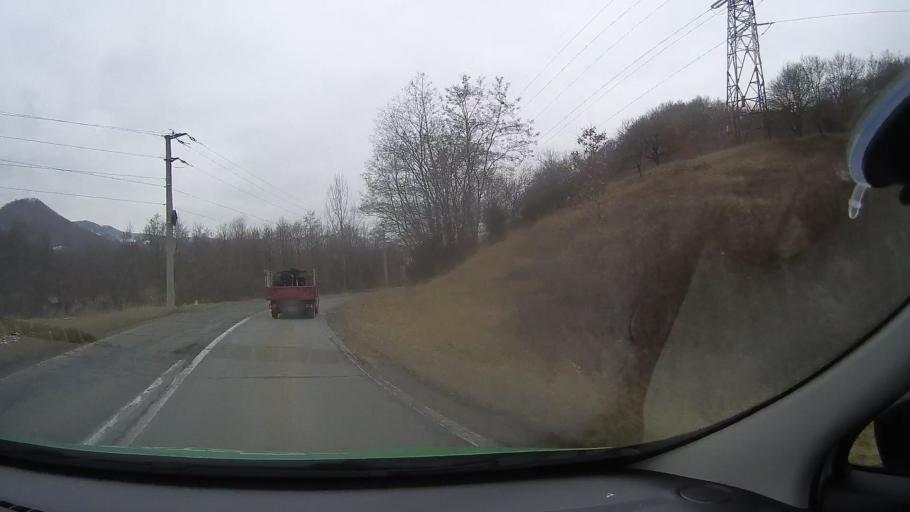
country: RO
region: Alba
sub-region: Comuna Ighiu
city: Ighiel
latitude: 46.1078
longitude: 23.4844
